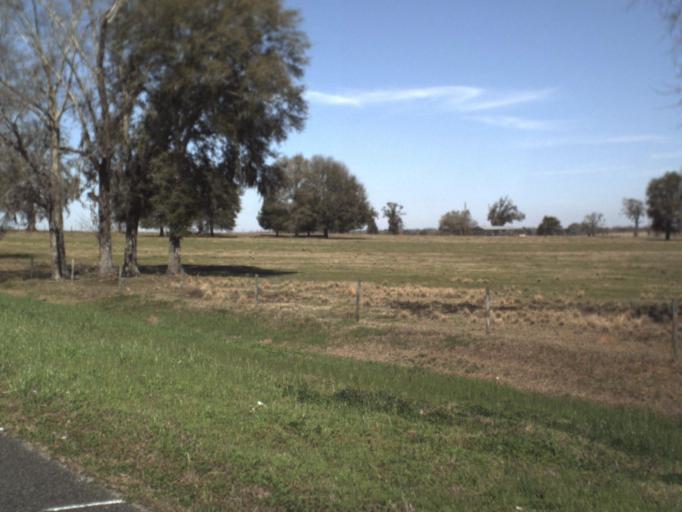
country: US
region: Florida
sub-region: Jackson County
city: Graceville
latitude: 30.9070
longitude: -85.3764
